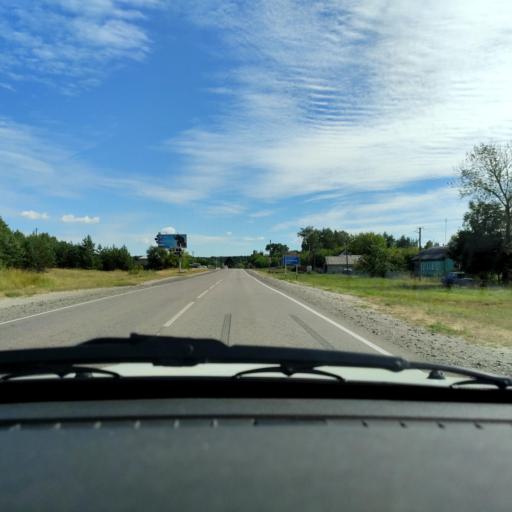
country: RU
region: Voronezj
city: Uglyanets
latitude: 51.8525
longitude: 39.6621
